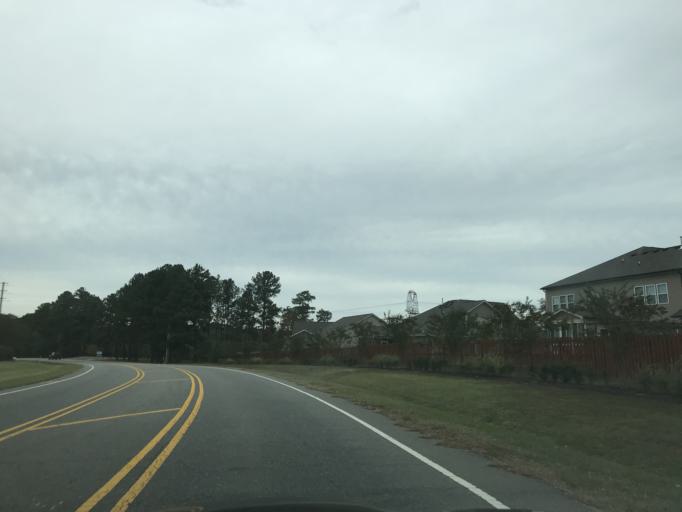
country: US
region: North Carolina
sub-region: Wake County
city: Rolesville
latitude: 35.9110
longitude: -78.5045
